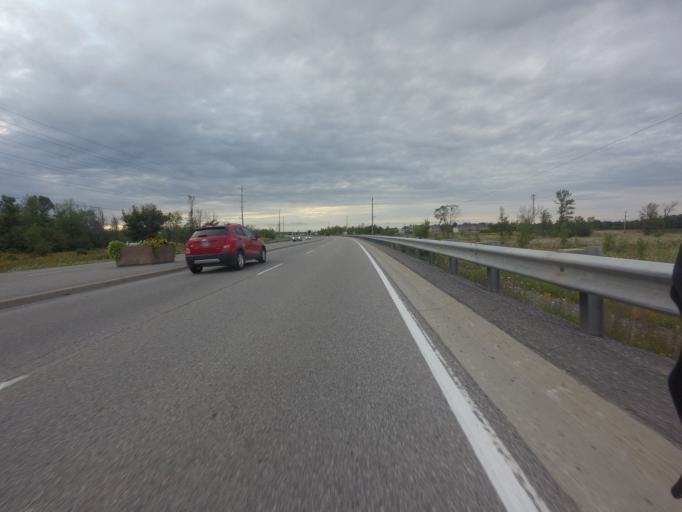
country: CA
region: Ontario
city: Carleton Place
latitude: 45.1367
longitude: -76.1237
